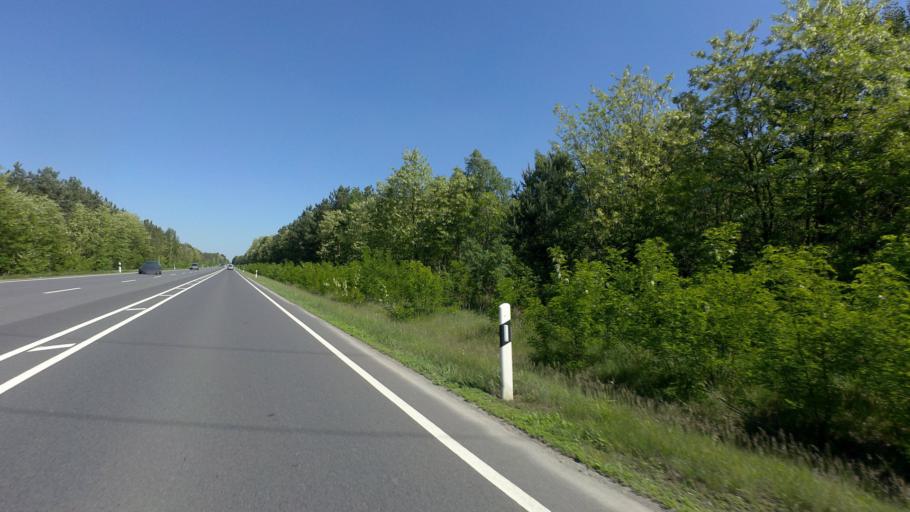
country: DE
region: Brandenburg
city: Spremberg
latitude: 51.6263
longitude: 14.3625
